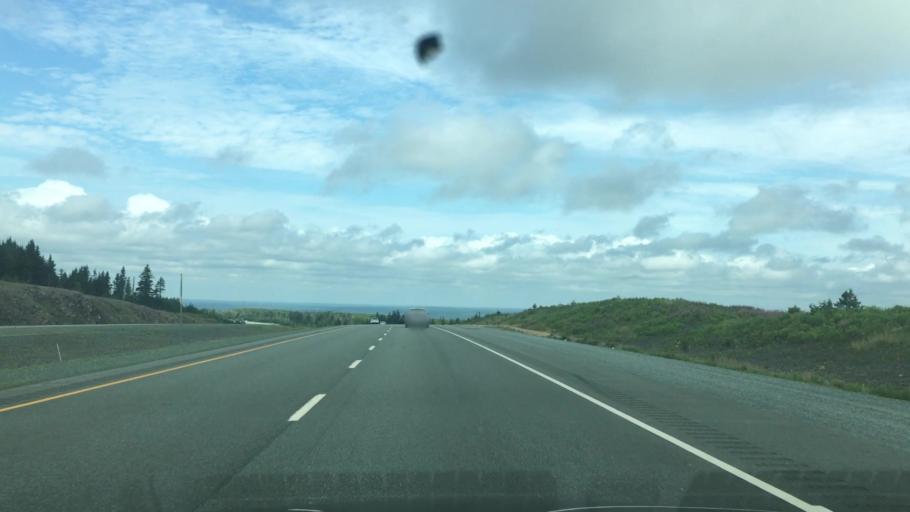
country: CA
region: Nova Scotia
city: Oxford
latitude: 45.5706
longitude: -63.7118
